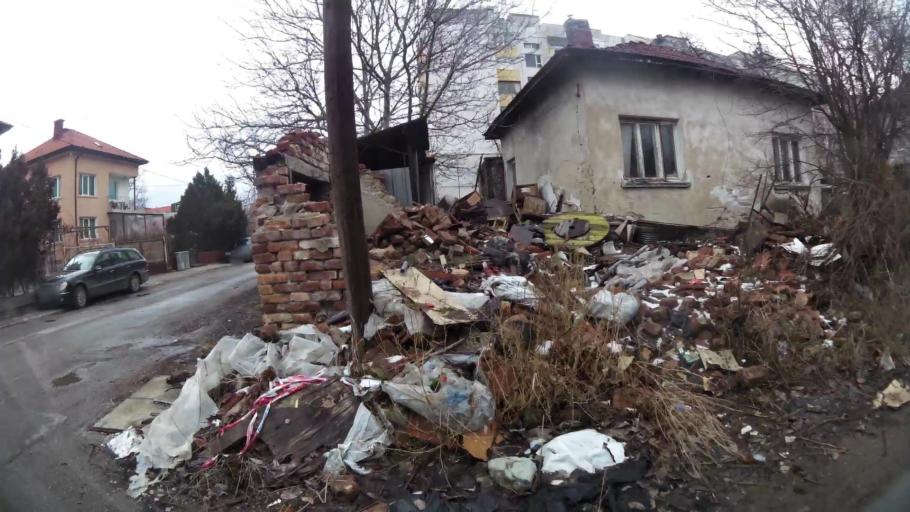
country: BG
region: Sofiya
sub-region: Obshtina Bozhurishte
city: Bozhurishte
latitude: 42.7389
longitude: 23.2672
